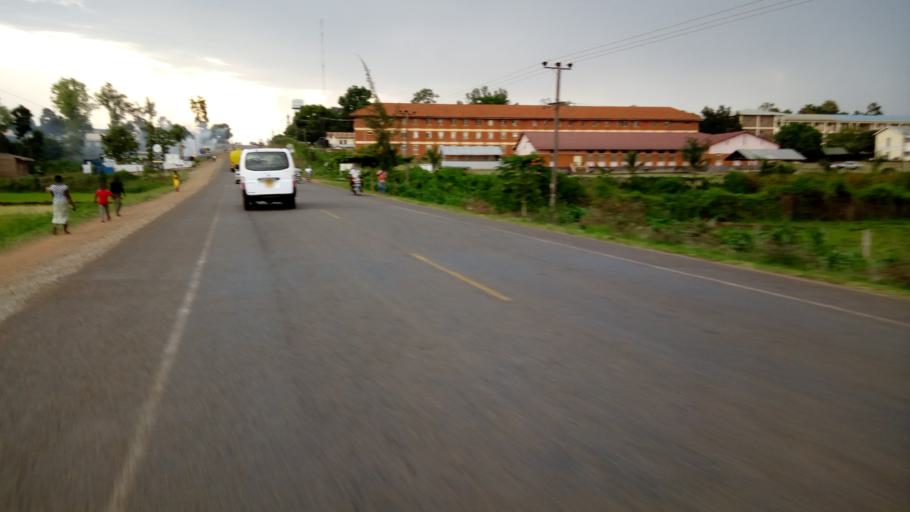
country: UG
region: Eastern Region
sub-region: Mbale District
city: Mbale
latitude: 1.1025
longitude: 34.1742
